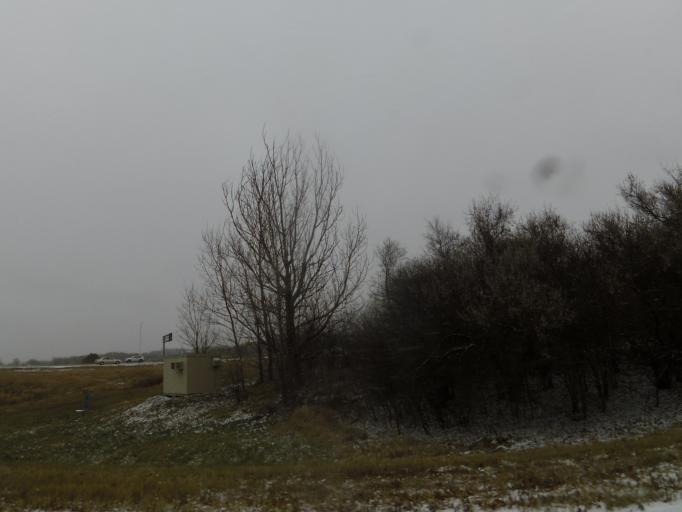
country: US
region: Minnesota
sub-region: Dakota County
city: Apple Valley
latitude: 44.7797
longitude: -93.2189
